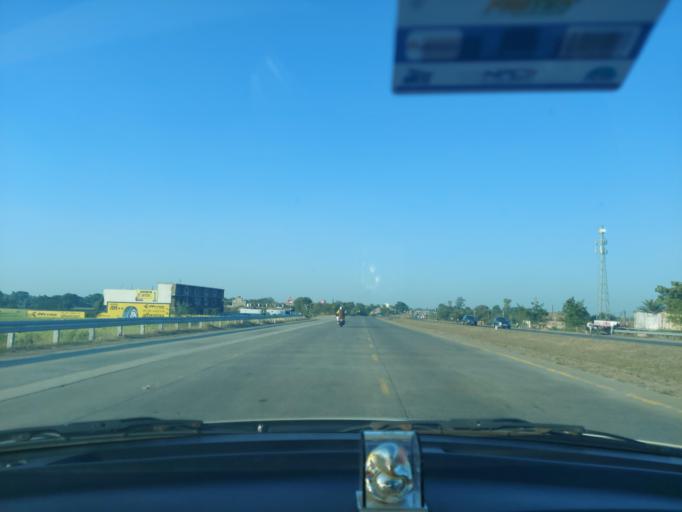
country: IN
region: Madhya Pradesh
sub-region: Shajapur
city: Maksi
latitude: 23.1729
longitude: 76.1528
